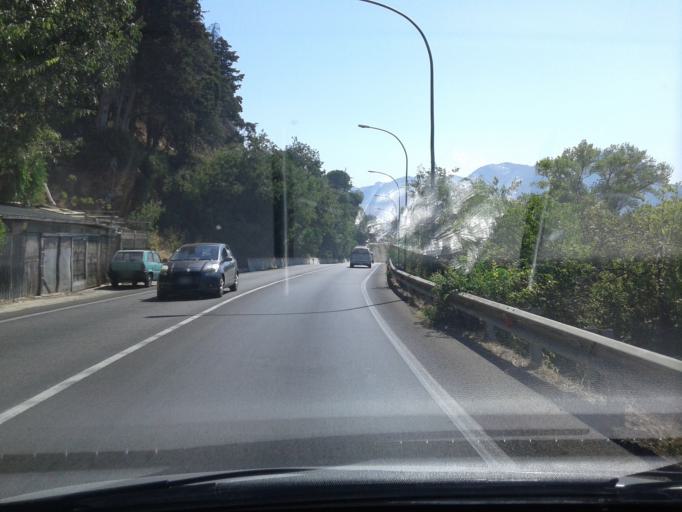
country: IT
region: Sicily
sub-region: Palermo
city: Cannizzaro-Favara
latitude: 38.0718
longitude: 13.2727
